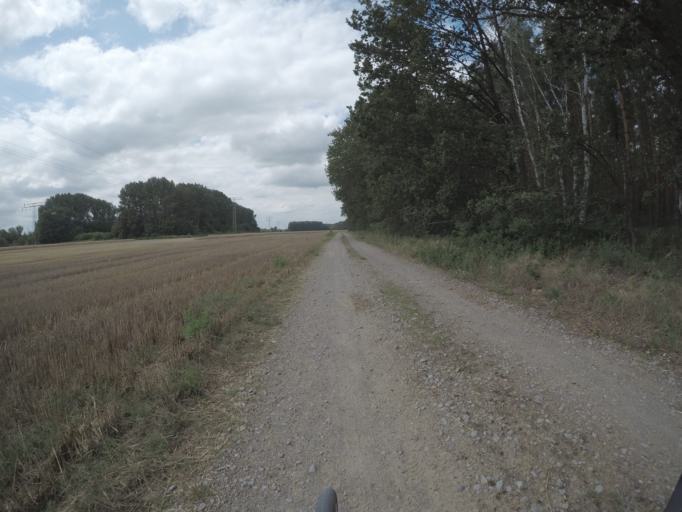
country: DE
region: Brandenburg
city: Brieselang
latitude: 52.6131
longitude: 13.0389
